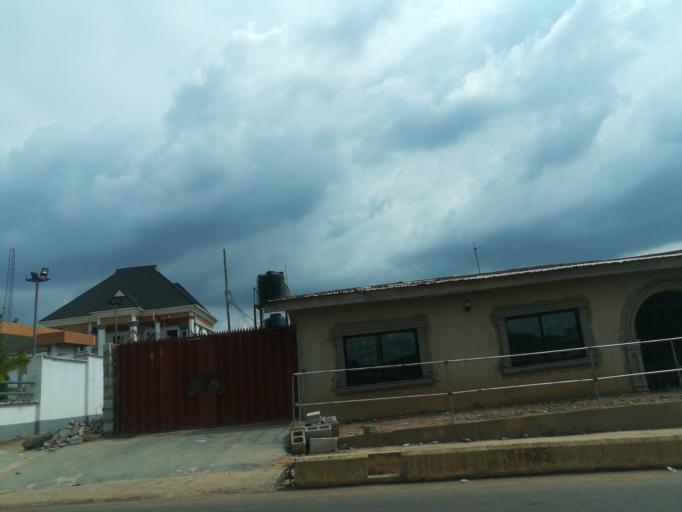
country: NG
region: Oyo
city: Ibadan
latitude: 7.4174
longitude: 3.8563
